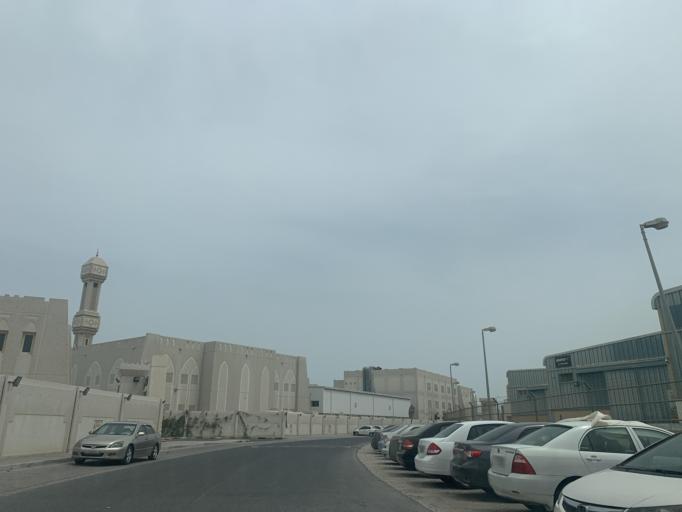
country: BH
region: Muharraq
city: Al Hadd
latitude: 26.2184
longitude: 50.6517
